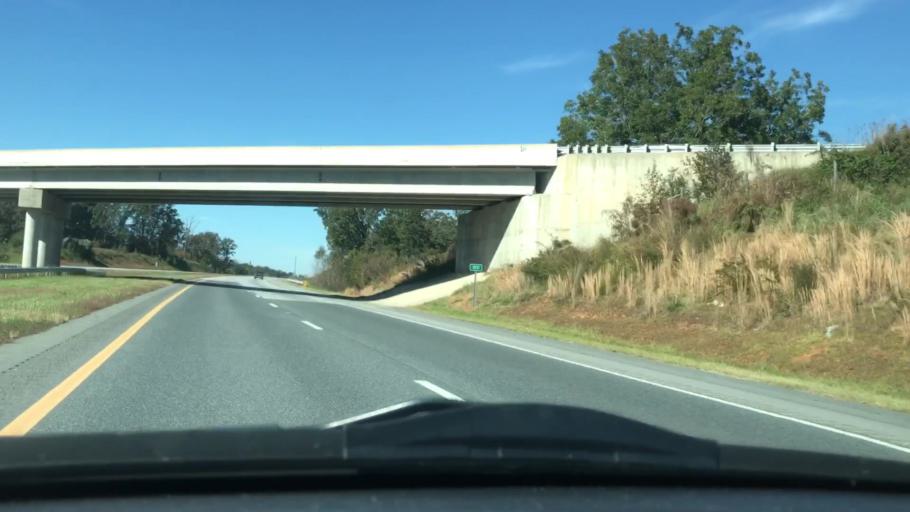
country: US
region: North Carolina
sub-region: Randolph County
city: Randleman
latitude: 35.8553
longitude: -79.8814
